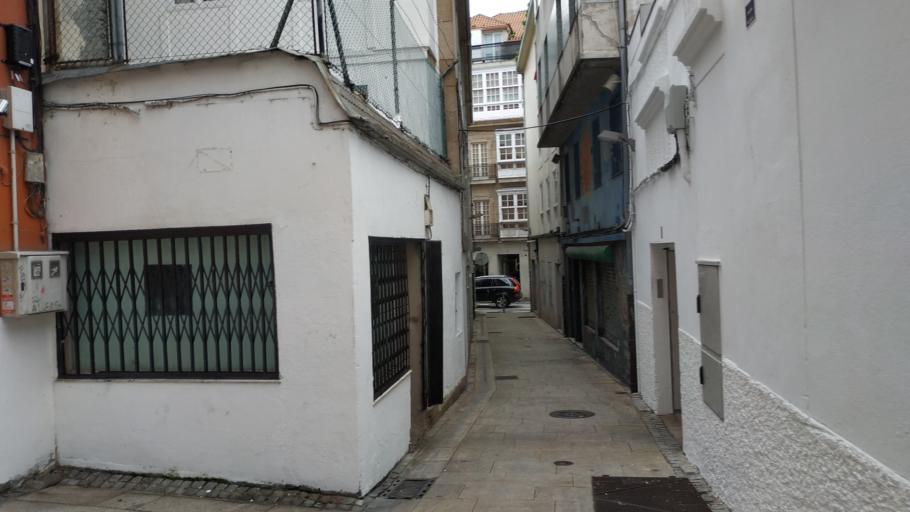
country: ES
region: Galicia
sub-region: Provincia da Coruna
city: A Coruna
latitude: 43.3715
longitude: -8.4009
